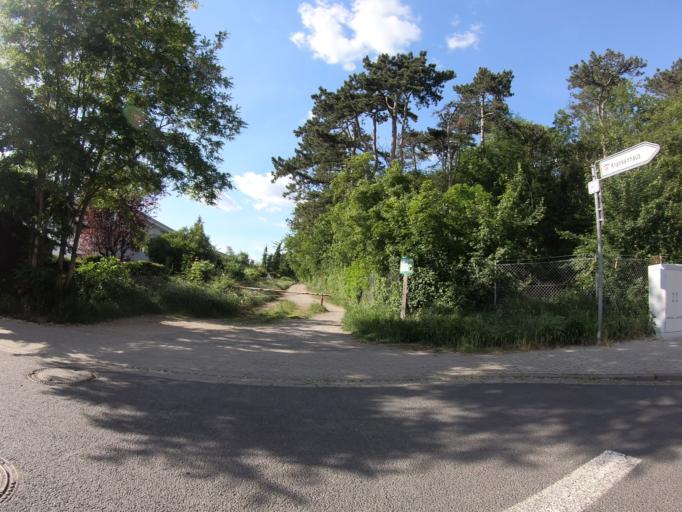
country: DE
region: Lower Saxony
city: Wolfenbuettel
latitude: 52.1812
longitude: 10.5307
